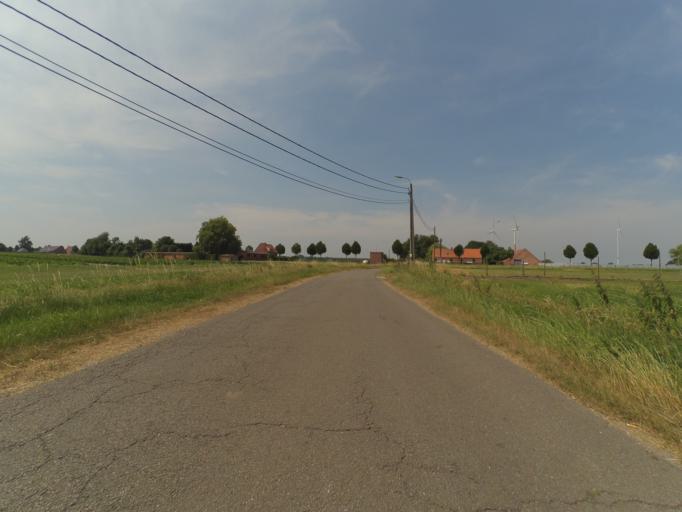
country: BE
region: Flanders
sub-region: Provincie Antwerpen
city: Hoogstraten
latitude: 51.4621
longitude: 4.7365
